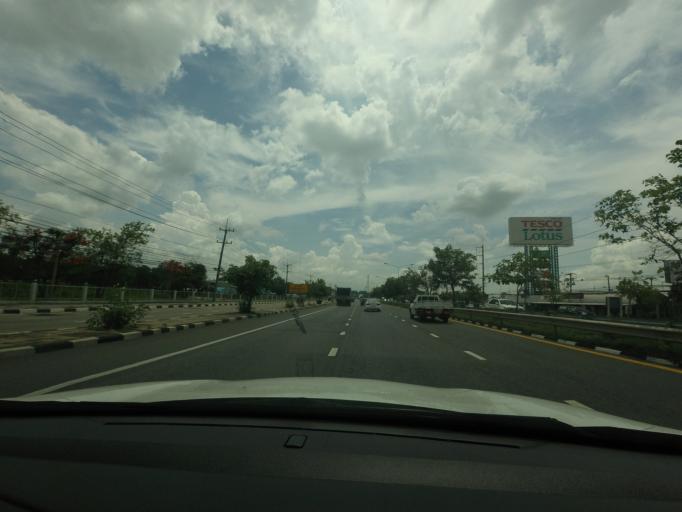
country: TH
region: Sara Buri
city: Saraburi
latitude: 14.5206
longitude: 100.9241
